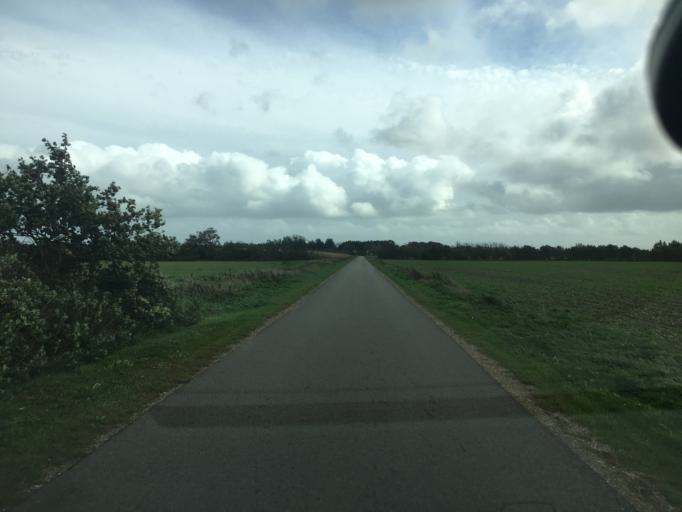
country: DK
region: South Denmark
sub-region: Tonder Kommune
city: Sherrebek
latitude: 55.0777
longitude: 8.8191
